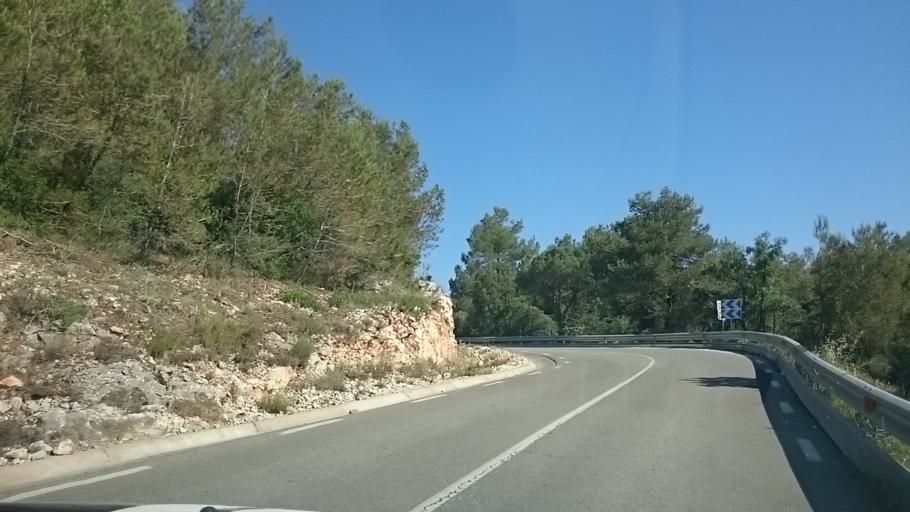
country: ES
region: Catalonia
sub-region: Provincia de Tarragona
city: Querol
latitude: 41.4189
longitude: 1.5001
